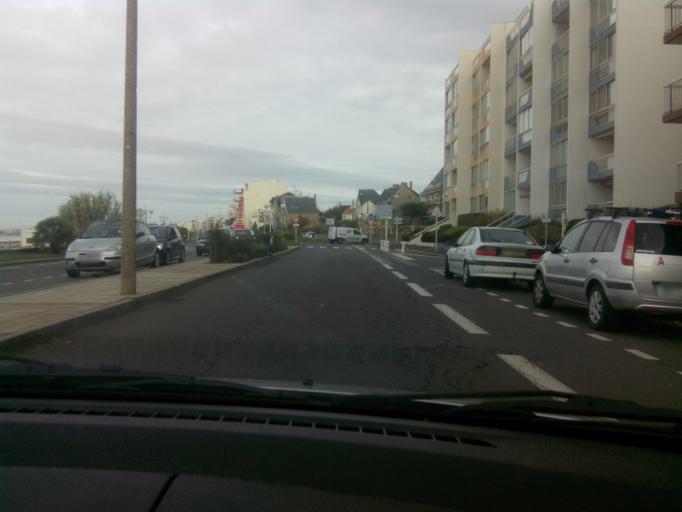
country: FR
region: Pays de la Loire
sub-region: Departement de la Loire-Atlantique
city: Pornichet
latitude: 47.2607
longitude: -2.3412
